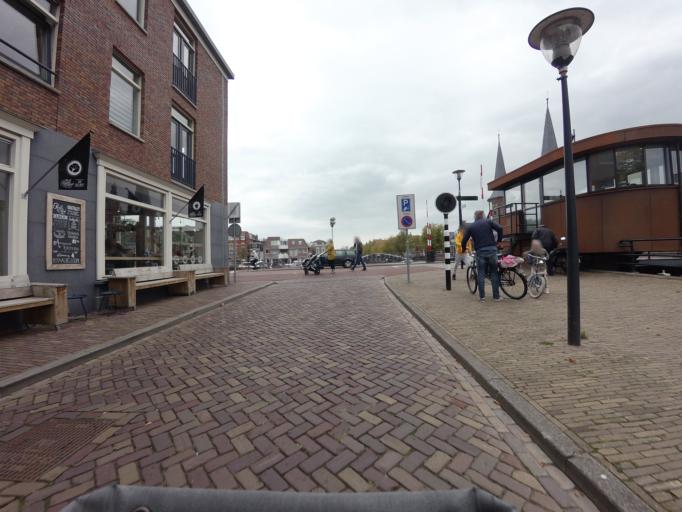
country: NL
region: Friesland
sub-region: Sudwest Fryslan
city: Sneek
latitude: 53.0289
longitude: 5.6590
